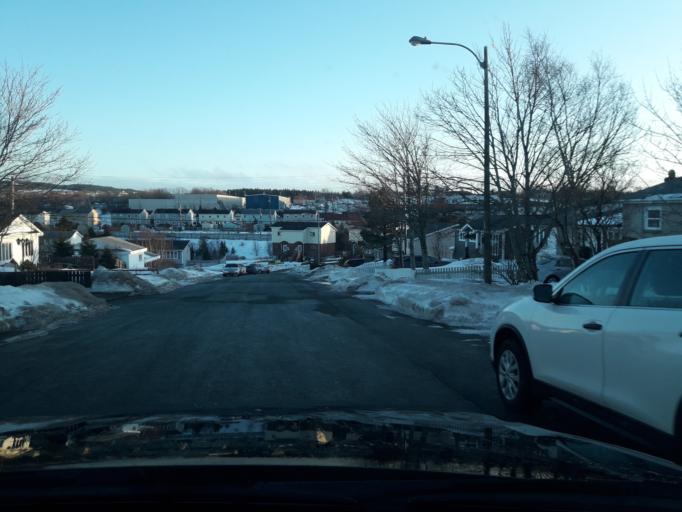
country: CA
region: Newfoundland and Labrador
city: Mount Pearl
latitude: 47.5237
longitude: -52.7700
